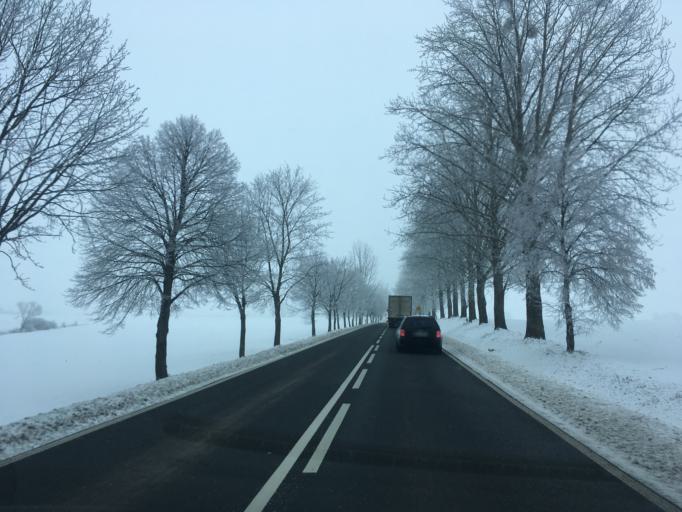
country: PL
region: Warmian-Masurian Voivodeship
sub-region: Powiat dzialdowski
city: Lidzbark
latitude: 53.2439
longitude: 19.9238
